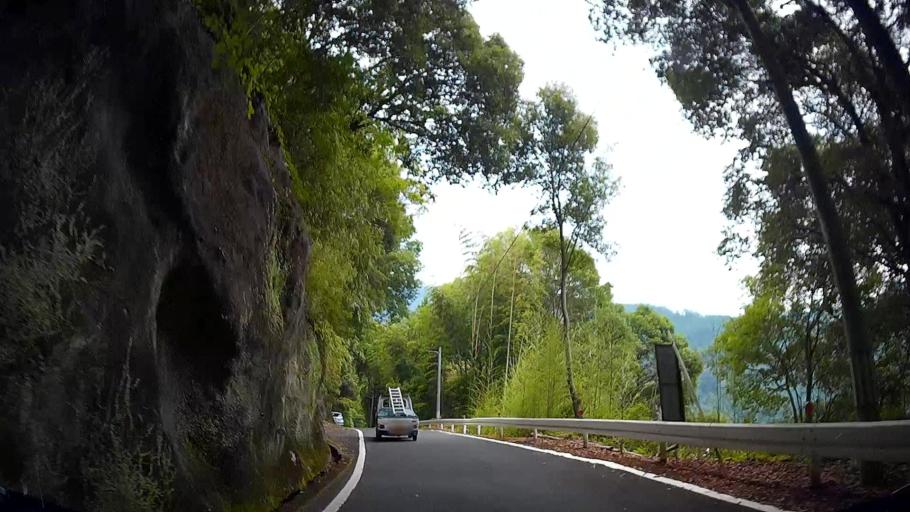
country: JP
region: Shizuoka
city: Hamakita
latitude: 35.0810
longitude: 137.7947
